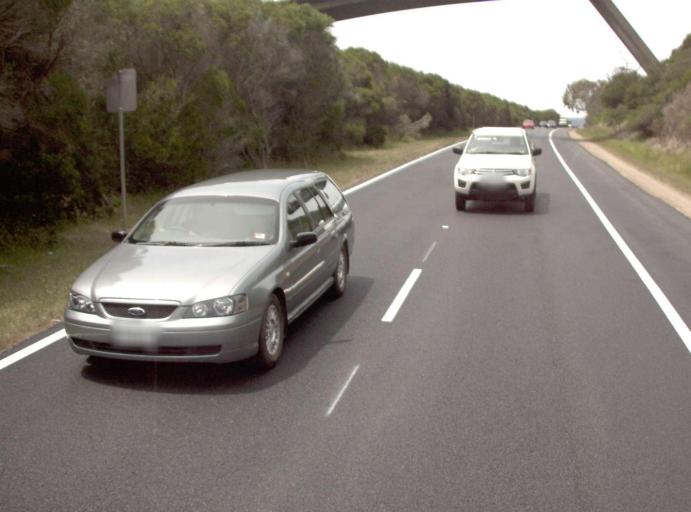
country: AU
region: Victoria
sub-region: Mornington Peninsula
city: McCrae
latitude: -38.3465
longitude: 144.9428
